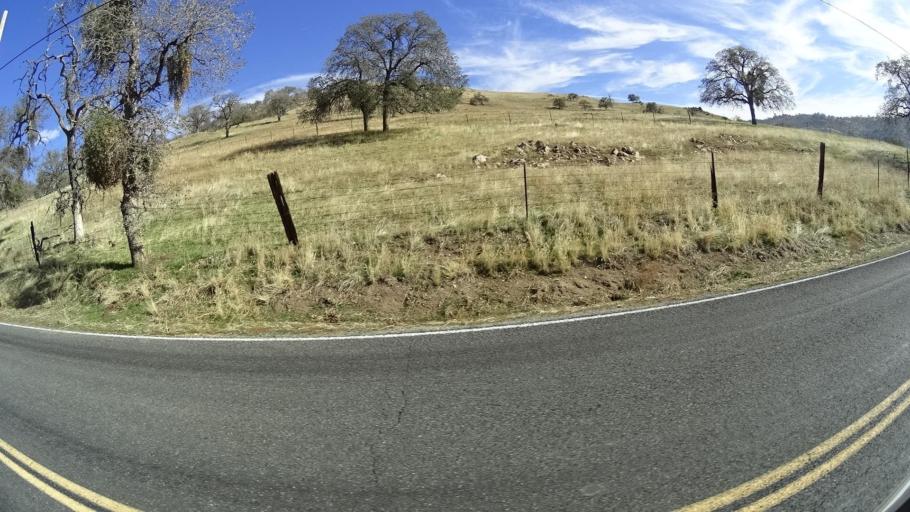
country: US
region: California
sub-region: Kern County
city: Alta Sierra
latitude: 35.6327
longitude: -118.8006
